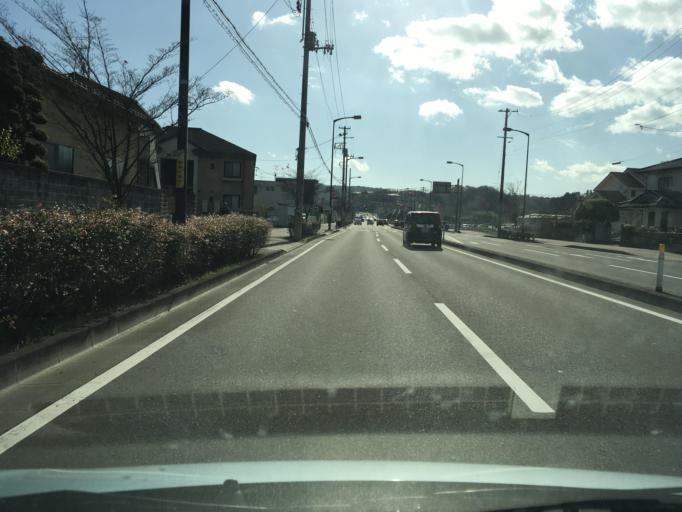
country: JP
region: Miyagi
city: Sendai
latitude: 38.2707
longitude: 140.7617
